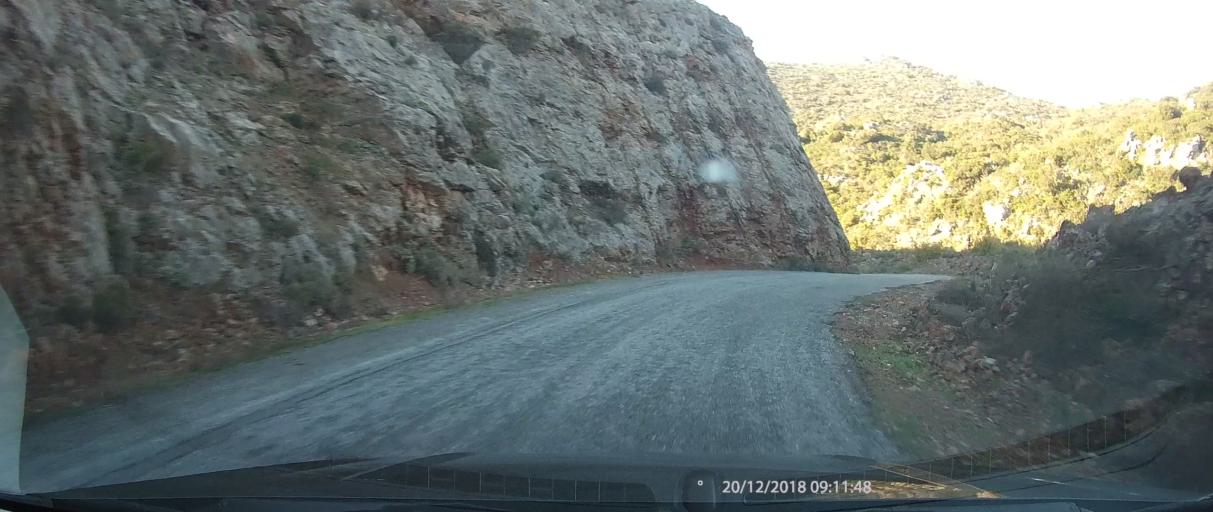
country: GR
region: Peloponnese
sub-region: Nomos Lakonias
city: Sykea
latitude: 36.9099
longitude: 22.9965
